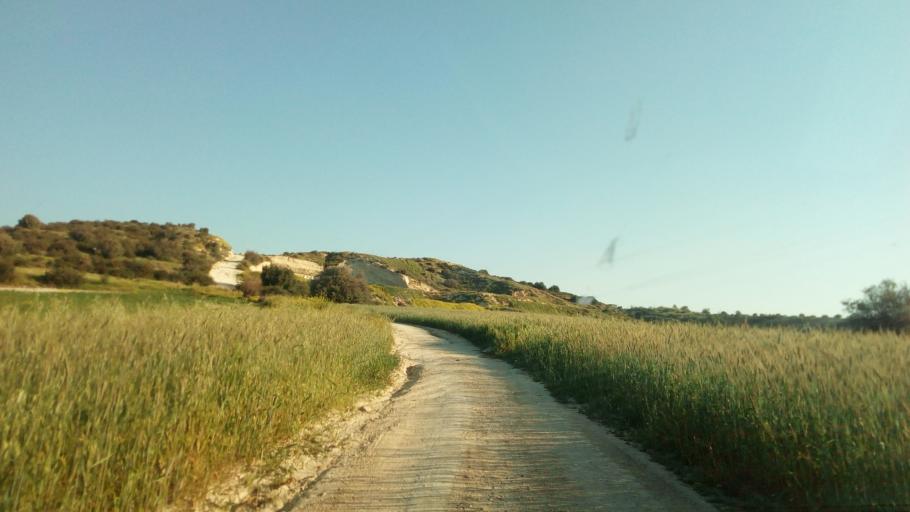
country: CY
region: Larnaka
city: Kofinou
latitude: 34.8415
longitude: 33.4488
